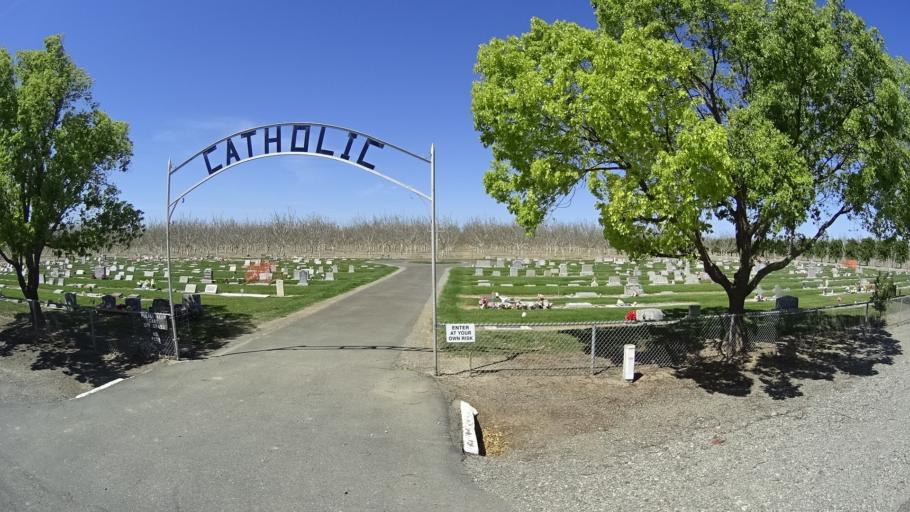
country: US
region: California
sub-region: Glenn County
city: Orland
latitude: 39.7029
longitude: -122.1406
